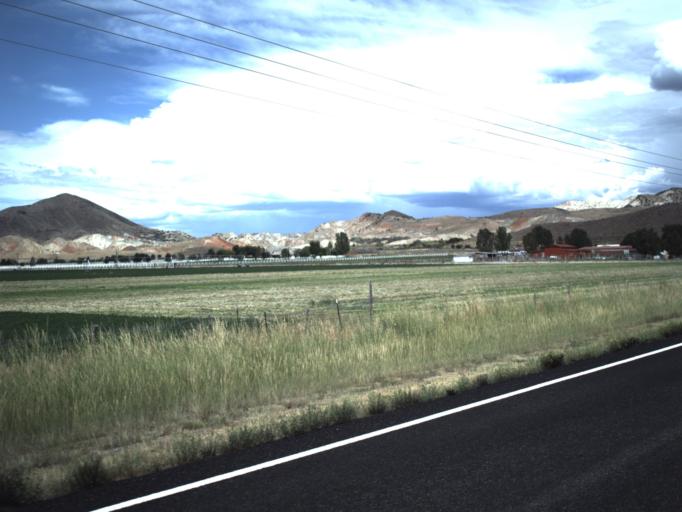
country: US
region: Utah
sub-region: Sevier County
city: Richfield
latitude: 38.7745
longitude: -111.9937
